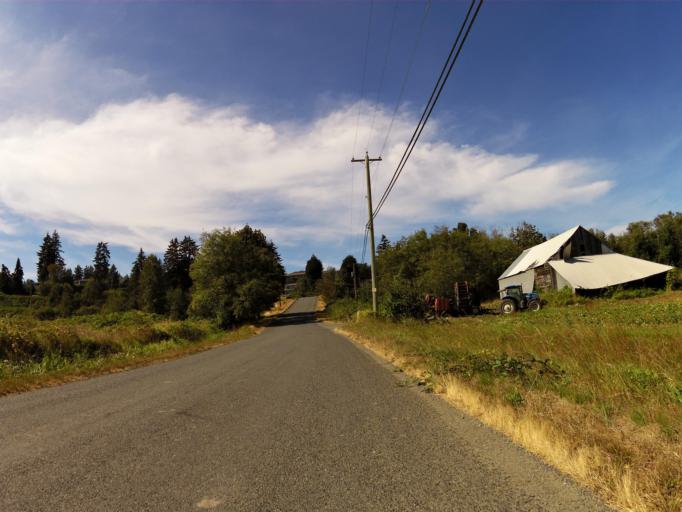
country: CA
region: British Columbia
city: North Saanich
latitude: 48.5612
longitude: -123.3929
